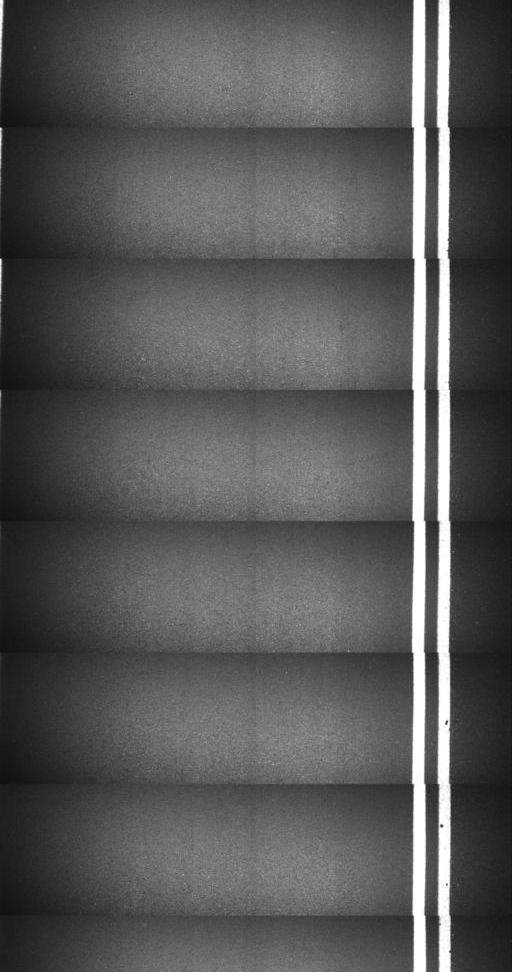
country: US
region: Vermont
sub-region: Orange County
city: Randolph
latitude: 43.8785
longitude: -72.6465
